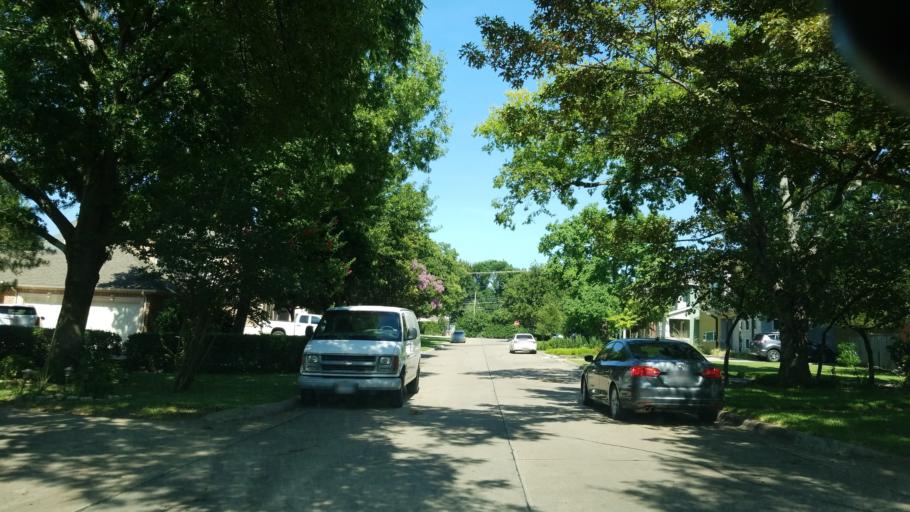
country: US
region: Texas
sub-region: Dallas County
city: Farmers Branch
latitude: 32.9229
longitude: -96.8887
